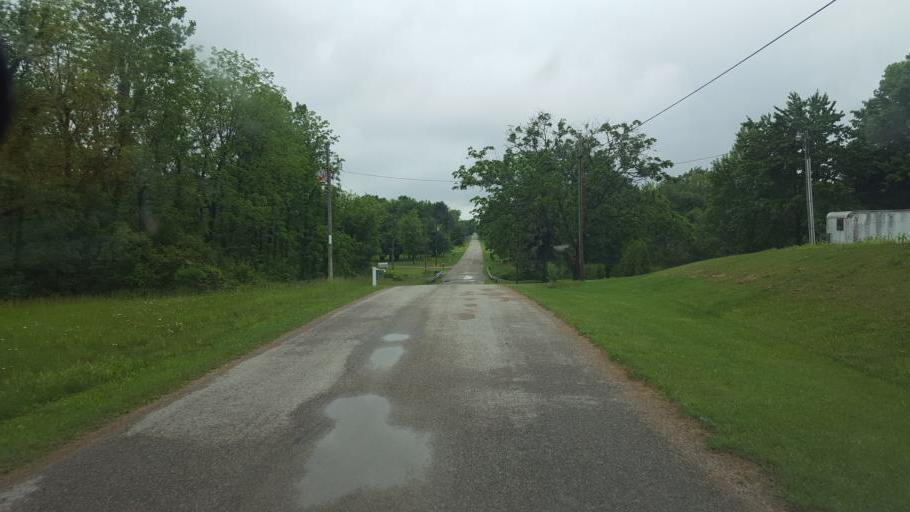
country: US
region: Ohio
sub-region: Morrow County
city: Mount Gilead
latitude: 40.4671
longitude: -82.7492
